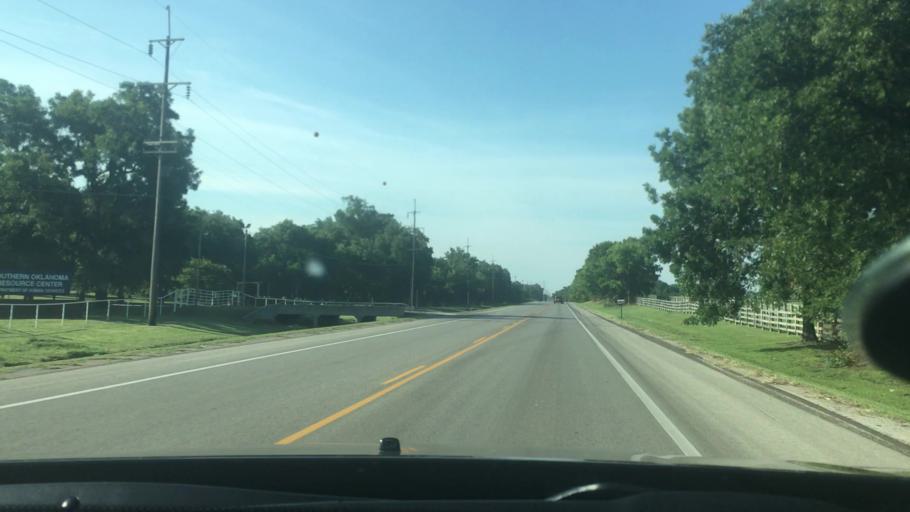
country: US
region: Oklahoma
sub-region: Garvin County
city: Pauls Valley
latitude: 34.6923
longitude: -97.2129
